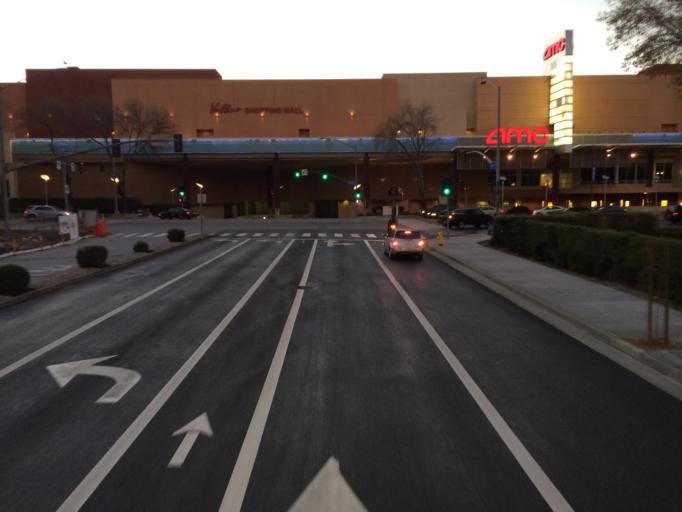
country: US
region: California
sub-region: Santa Clara County
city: Cupertino
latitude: 37.3256
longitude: -122.0135
